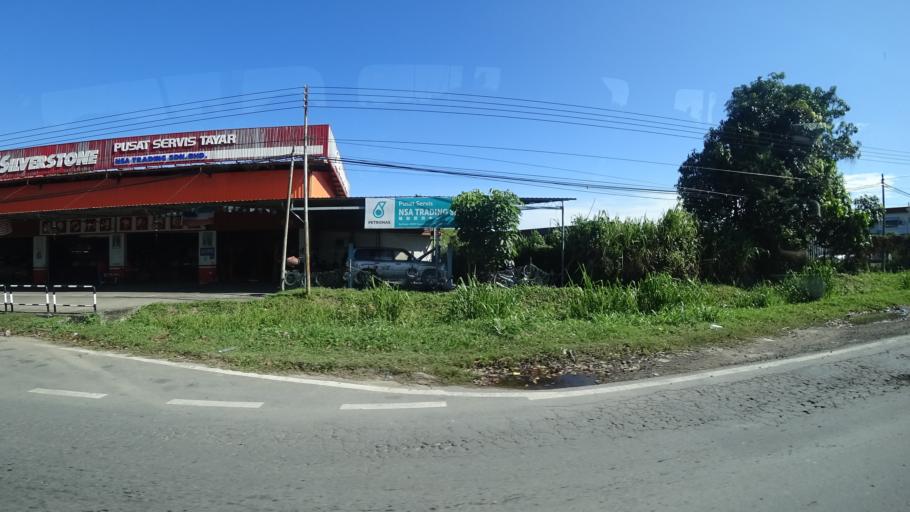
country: MY
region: Sabah
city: Kota Kinabalu
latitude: 6.1472
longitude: 116.2230
